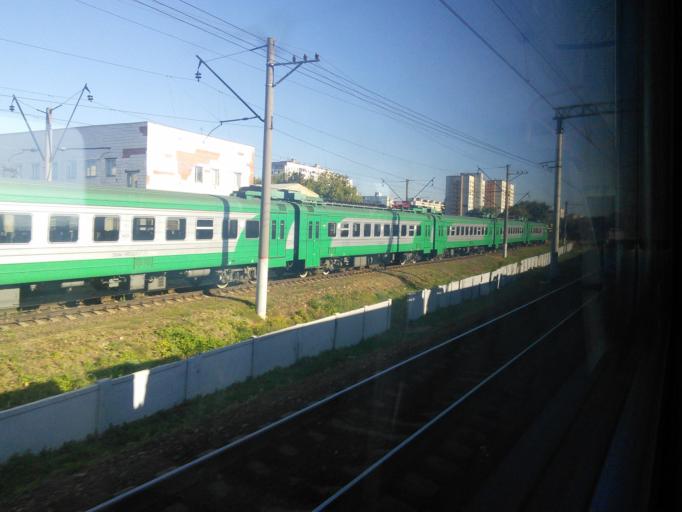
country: RU
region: Moscow
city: Mar'ino
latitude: 55.6680
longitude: 37.7244
